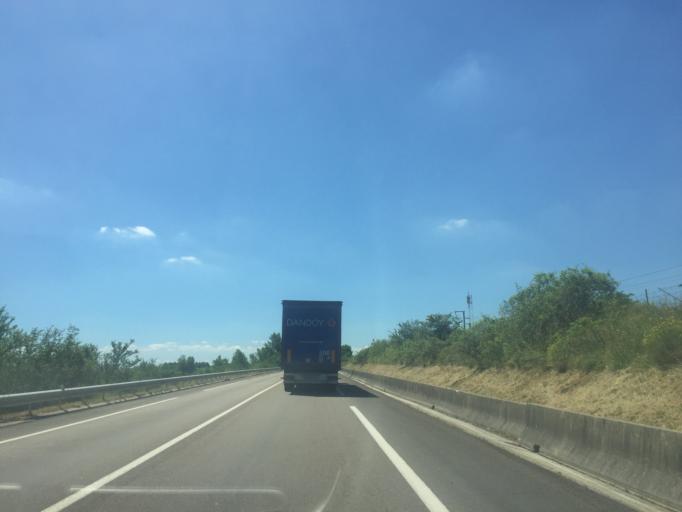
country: FR
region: Rhone-Alpes
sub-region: Departement du Rhone
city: Pusignan
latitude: 45.7622
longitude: 5.0832
